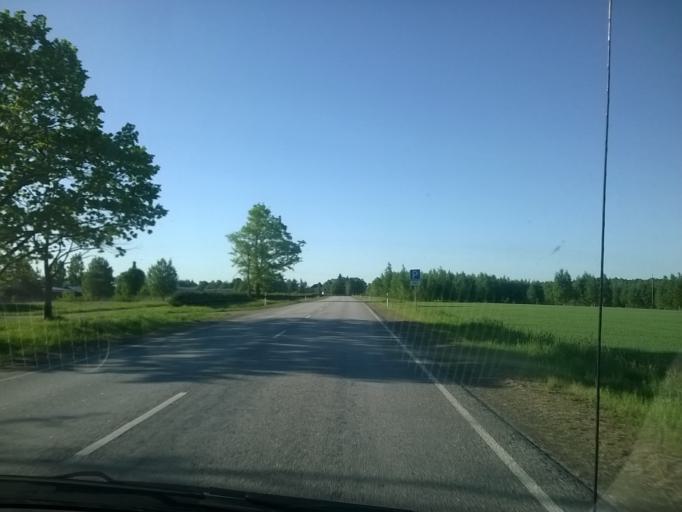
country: EE
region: Valgamaa
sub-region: Valga linn
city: Valga
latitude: 57.9320
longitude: 26.1725
